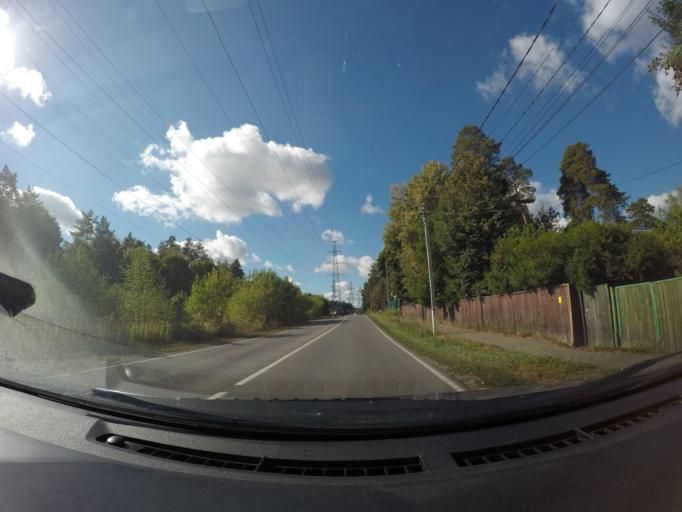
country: RU
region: Moskovskaya
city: Zhukovskiy
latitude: 55.6086
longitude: 38.1359
